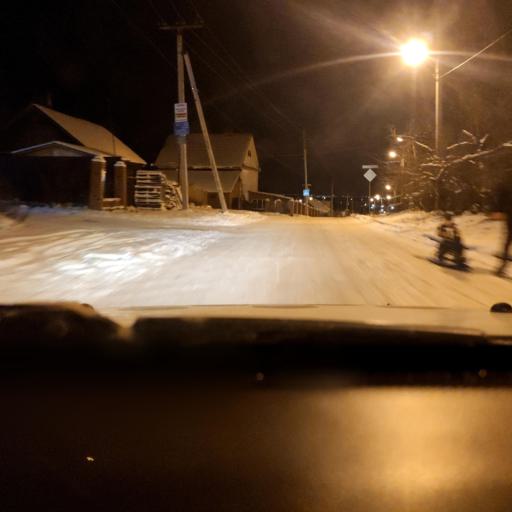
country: RU
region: Perm
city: Ferma
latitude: 57.9583
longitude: 56.3730
